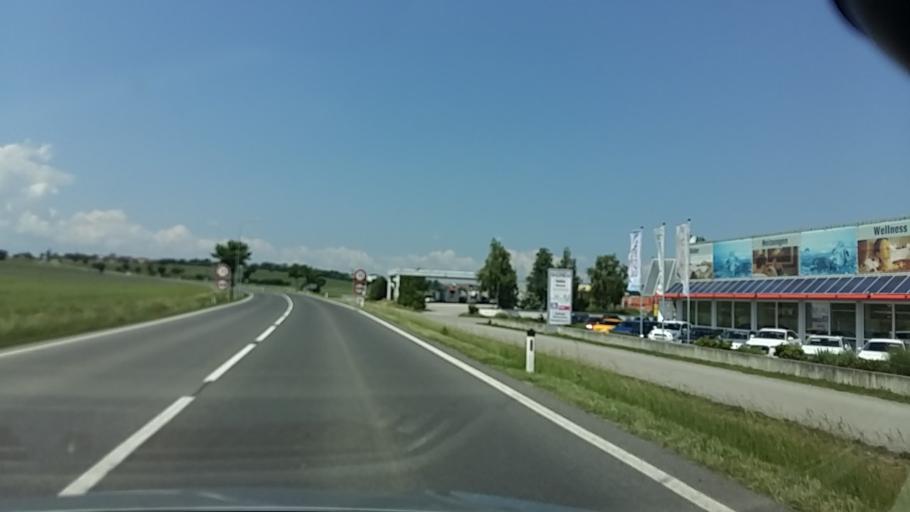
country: AT
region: Burgenland
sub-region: Politischer Bezirk Oberpullendorf
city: Horitschon
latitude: 47.5904
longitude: 16.5699
